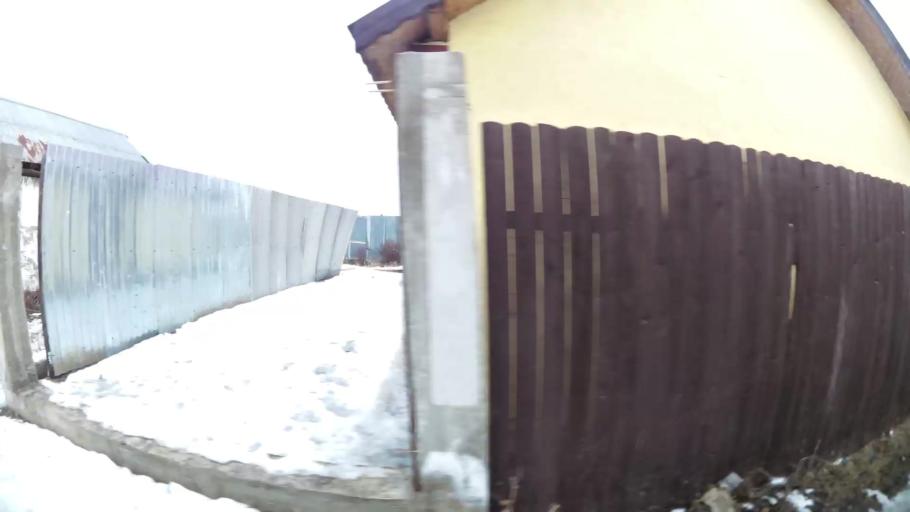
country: RO
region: Ilfov
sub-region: Comuna Pantelimon
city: Pantelimon
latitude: 44.4591
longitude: 26.1929
